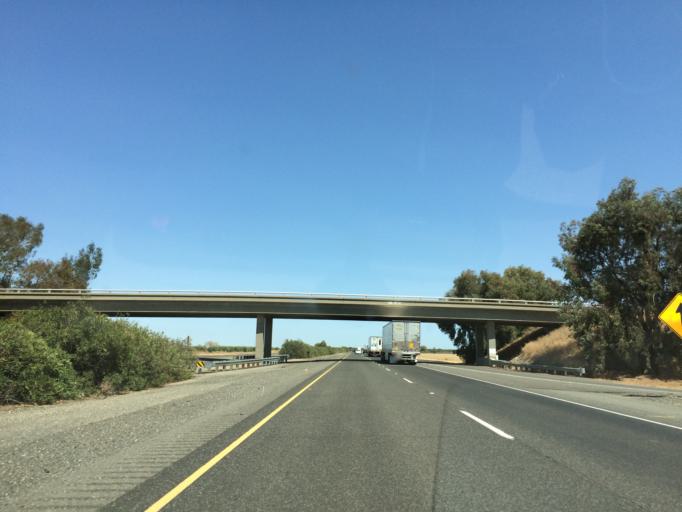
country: US
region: California
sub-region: Glenn County
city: Willows
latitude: 39.6234
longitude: -122.2052
